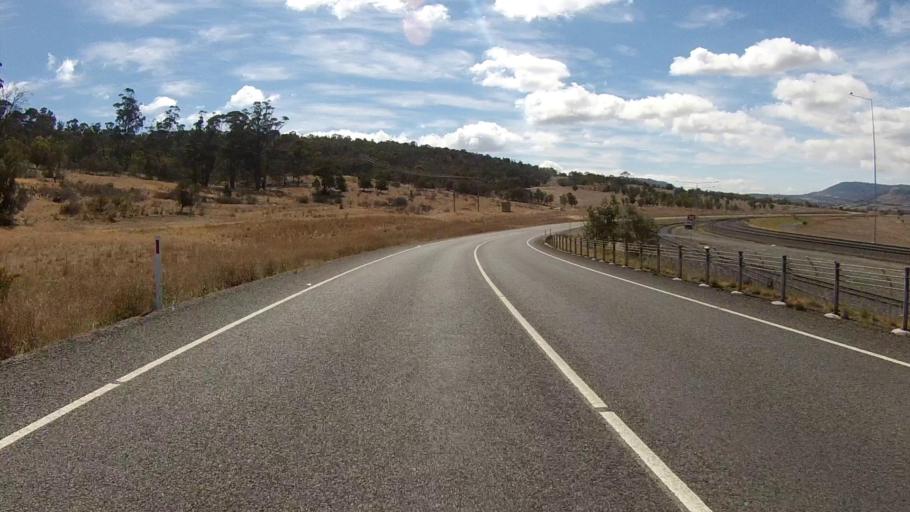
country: AU
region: Tasmania
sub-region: Brighton
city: Bridgewater
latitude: -42.7113
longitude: 147.2326
